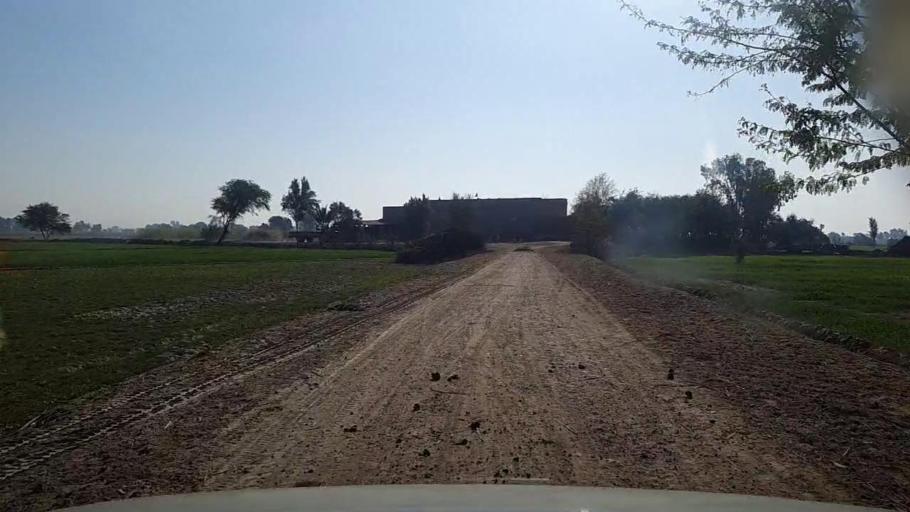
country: PK
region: Sindh
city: Khairpur
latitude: 28.0551
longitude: 69.7384
